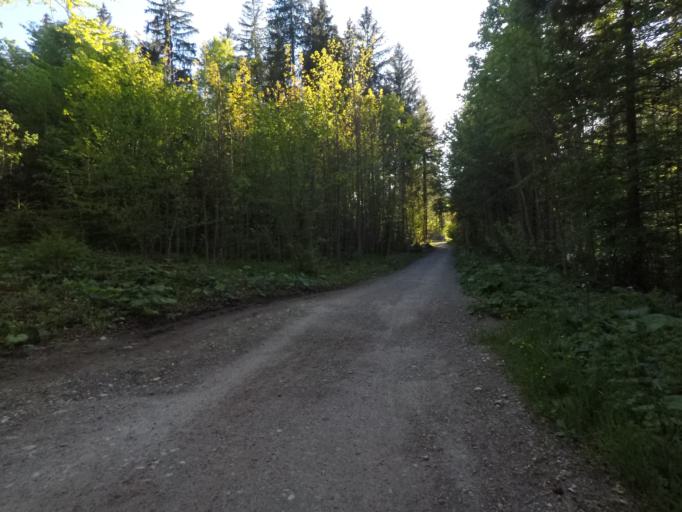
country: DE
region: Bavaria
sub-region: Upper Bavaria
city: Fischbachau
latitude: 47.7030
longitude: 11.9023
